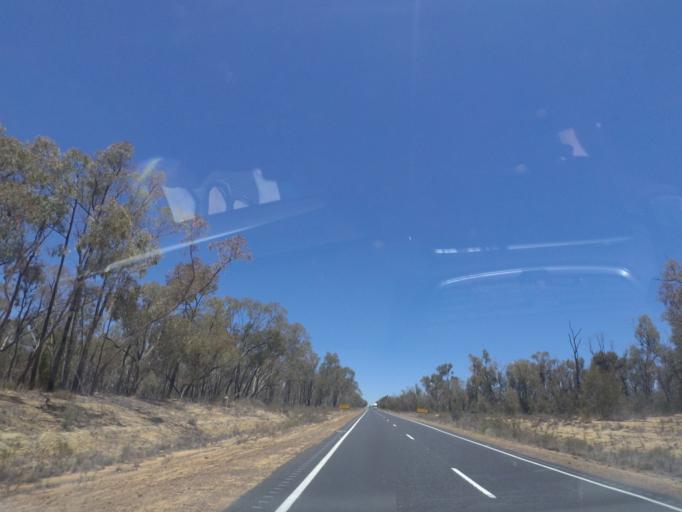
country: AU
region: New South Wales
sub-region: Warrumbungle Shire
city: Coonabarabran
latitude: -30.9538
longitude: 149.4209
